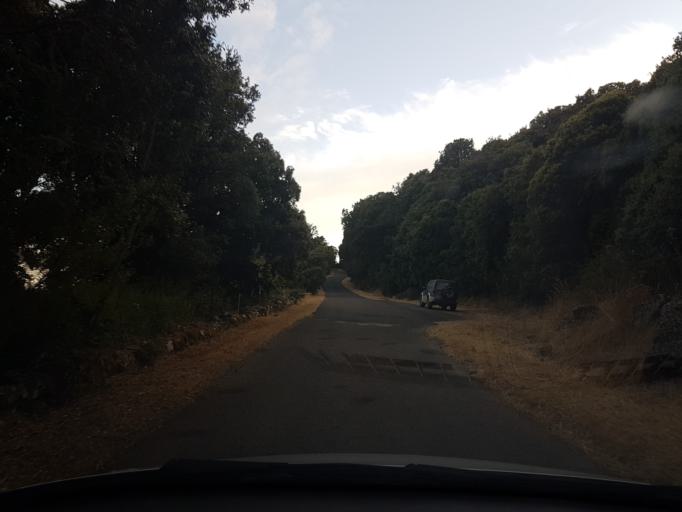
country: IT
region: Sardinia
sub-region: Provincia di Oristano
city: Seneghe
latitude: 40.1086
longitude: 8.5991
